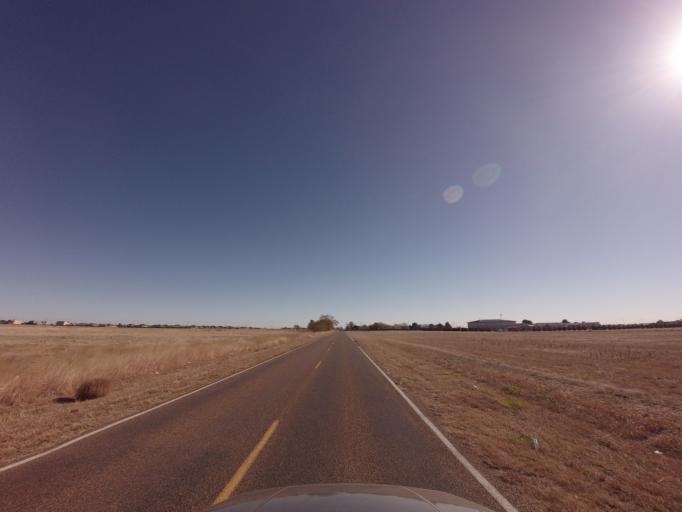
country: US
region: New Mexico
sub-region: Curry County
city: Clovis
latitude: 34.4194
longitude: -103.1649
